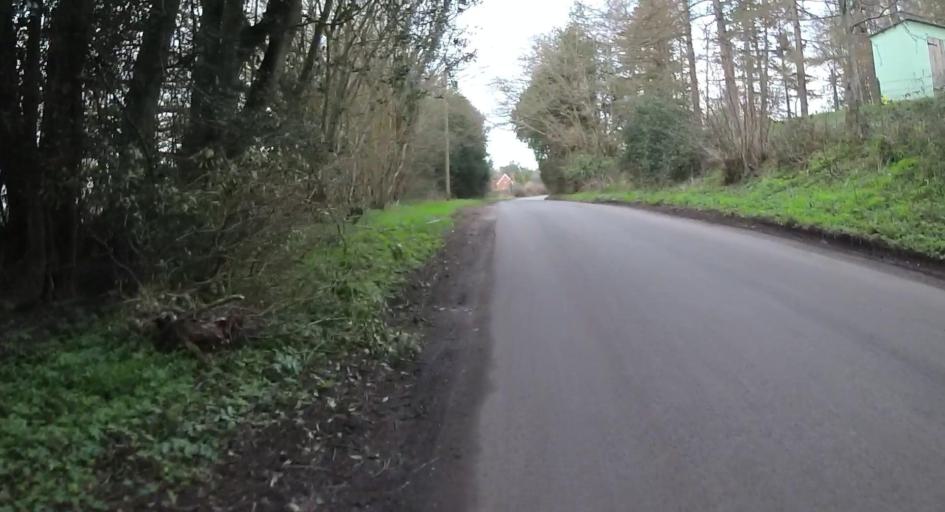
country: GB
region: England
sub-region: Hampshire
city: Lindford
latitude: 51.1410
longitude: -0.8184
